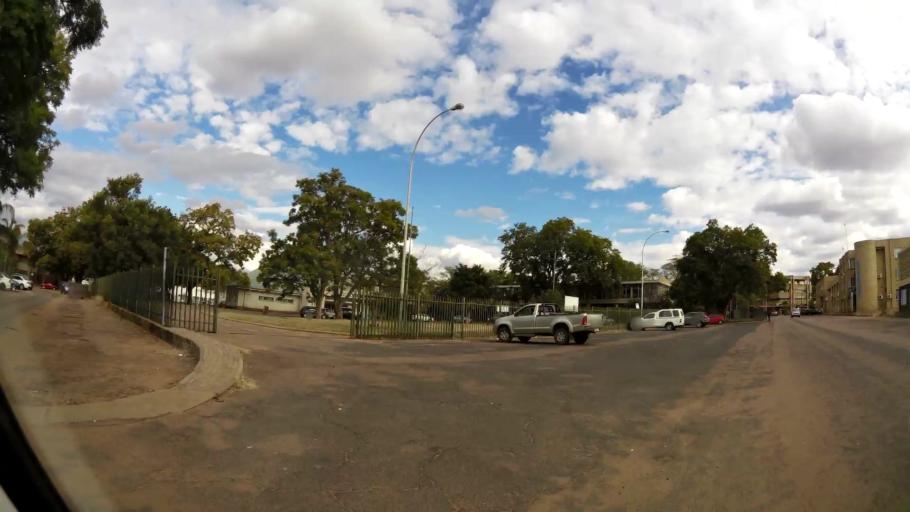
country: ZA
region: Limpopo
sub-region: Waterberg District Municipality
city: Modimolle
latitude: -24.7025
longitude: 28.4071
